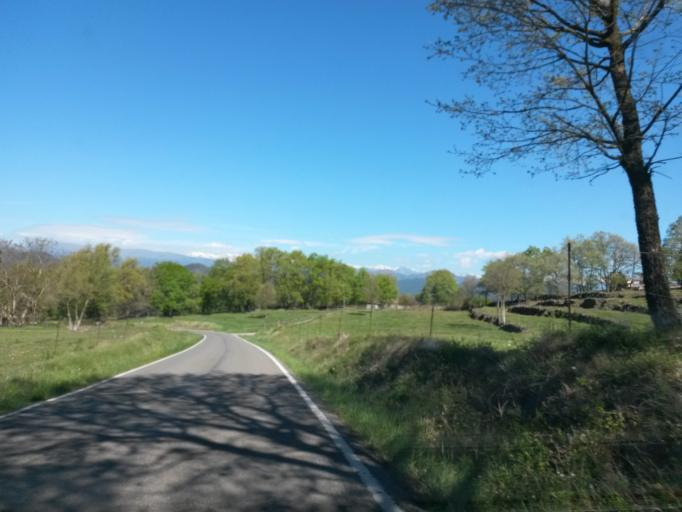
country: ES
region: Catalonia
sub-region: Provincia de Girona
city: Sant Cristofol de les Fonts
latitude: 42.1768
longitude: 2.5058
